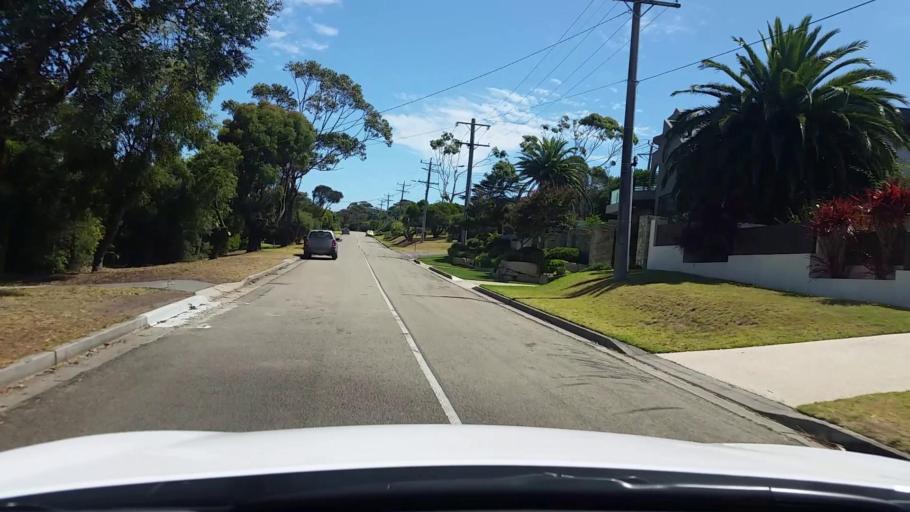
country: AU
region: Victoria
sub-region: Mornington Peninsula
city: Safety Beach
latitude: -38.3029
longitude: 144.9953
